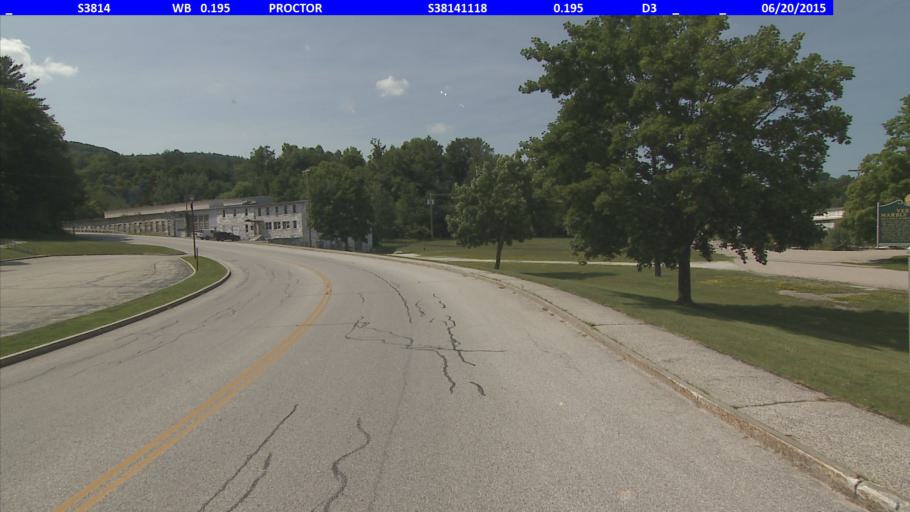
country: US
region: Vermont
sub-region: Rutland County
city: West Rutland
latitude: 43.6626
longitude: -73.0360
